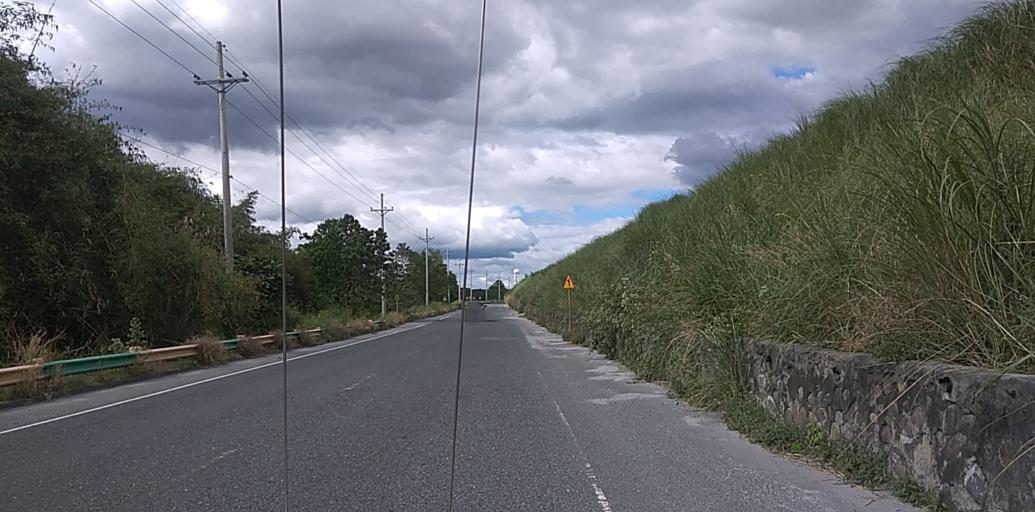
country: PH
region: Central Luzon
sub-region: Province of Pampanga
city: Dolores
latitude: 15.1039
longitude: 120.5221
